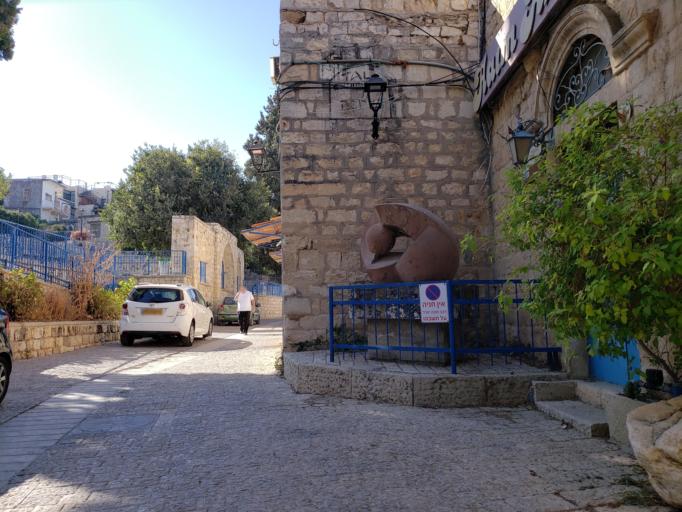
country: IL
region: Northern District
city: Safed
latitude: 32.9665
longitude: 35.4930
